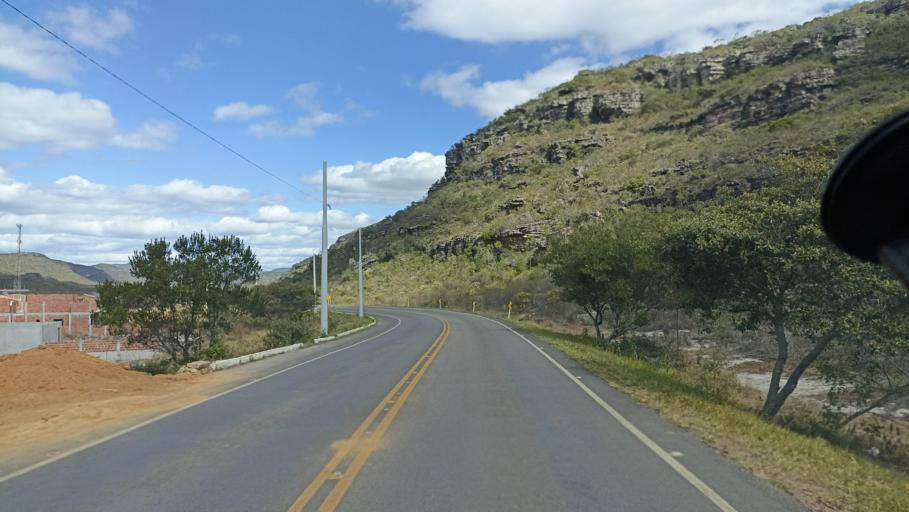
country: BR
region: Bahia
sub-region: Andarai
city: Vera Cruz
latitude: -13.0093
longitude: -41.3755
